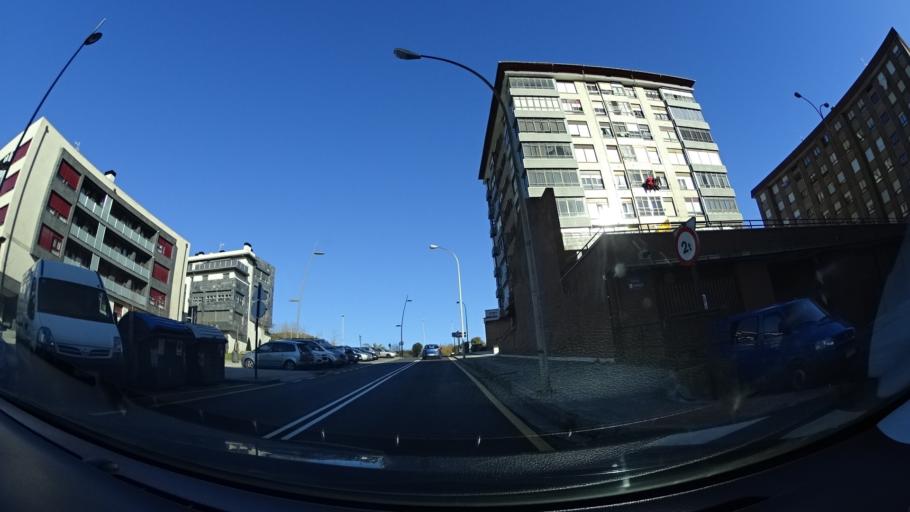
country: ES
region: Basque Country
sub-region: Bizkaia
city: Bermeo
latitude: 43.4208
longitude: -2.7300
